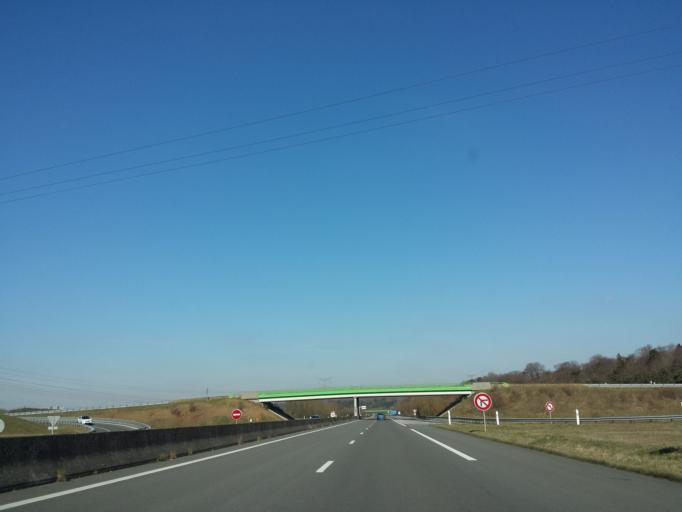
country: FR
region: Picardie
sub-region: Departement de la Somme
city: Conty
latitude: 49.7356
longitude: 2.2351
